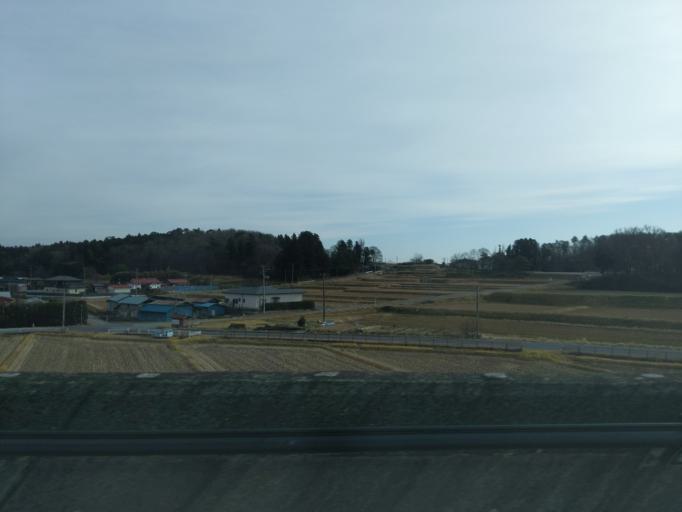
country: JP
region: Miyagi
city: Kogota
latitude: 38.7371
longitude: 141.0651
